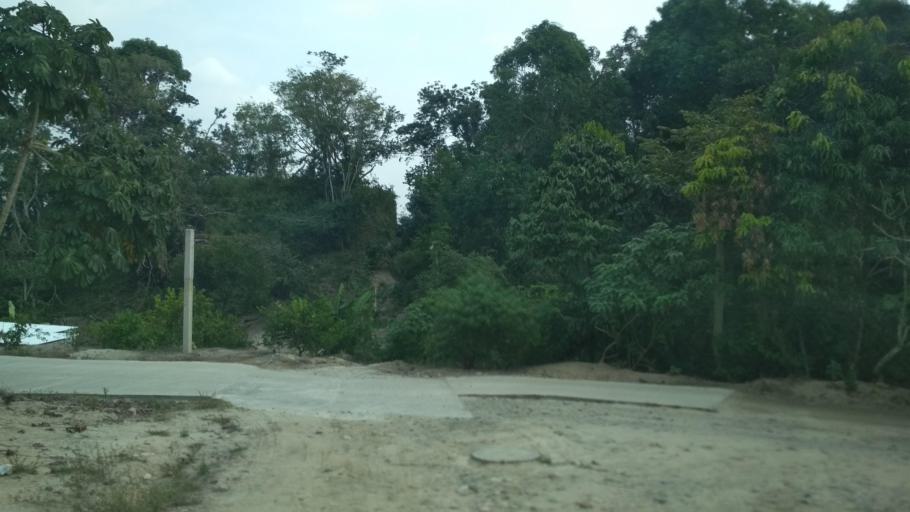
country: MM
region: Kayah
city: Loikaw
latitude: 20.2202
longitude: 97.2849
